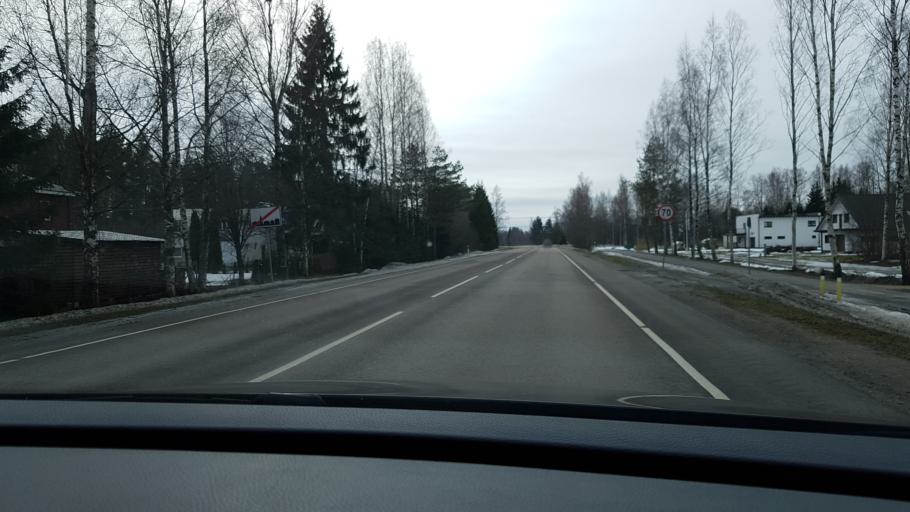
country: EE
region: Paernumaa
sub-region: Paikuse vald
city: Paikuse
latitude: 58.3939
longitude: 24.6446
